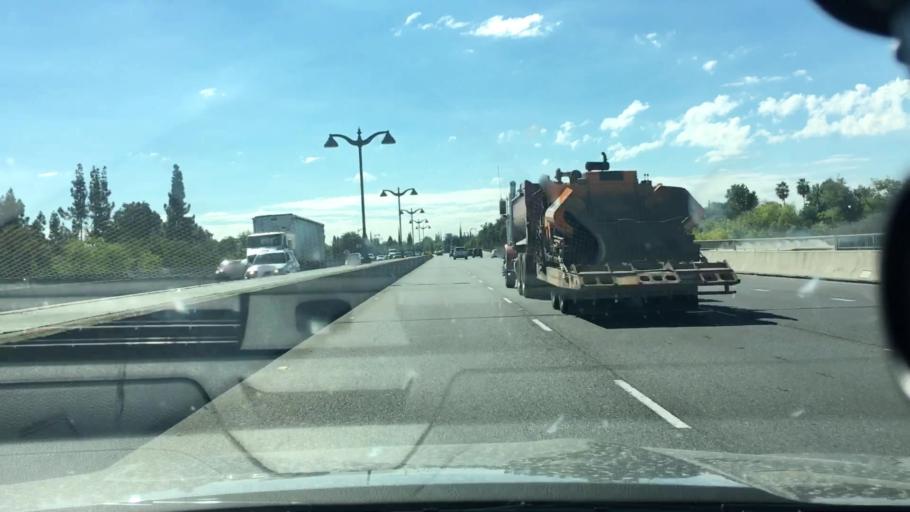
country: US
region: California
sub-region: Sacramento County
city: Rosemont
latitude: 38.5669
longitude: -121.3828
